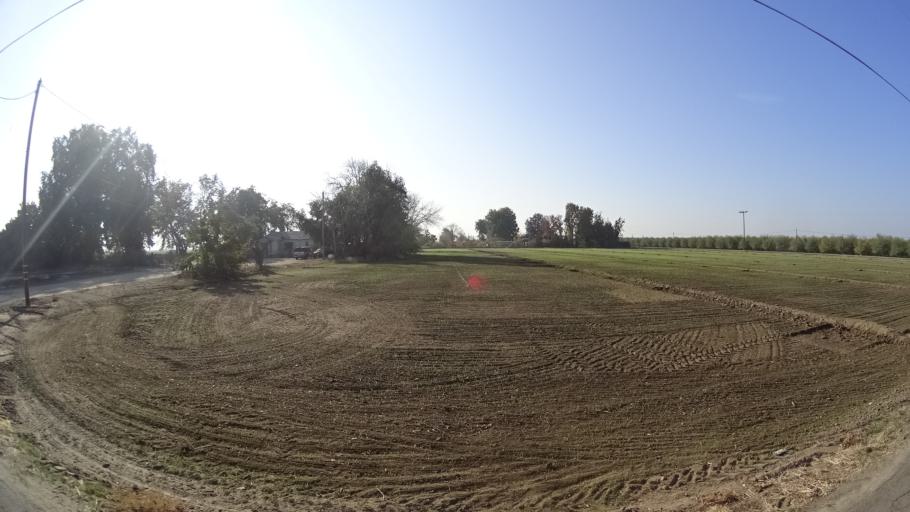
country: US
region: California
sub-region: Kern County
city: Greenfield
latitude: 35.2598
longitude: -119.0380
